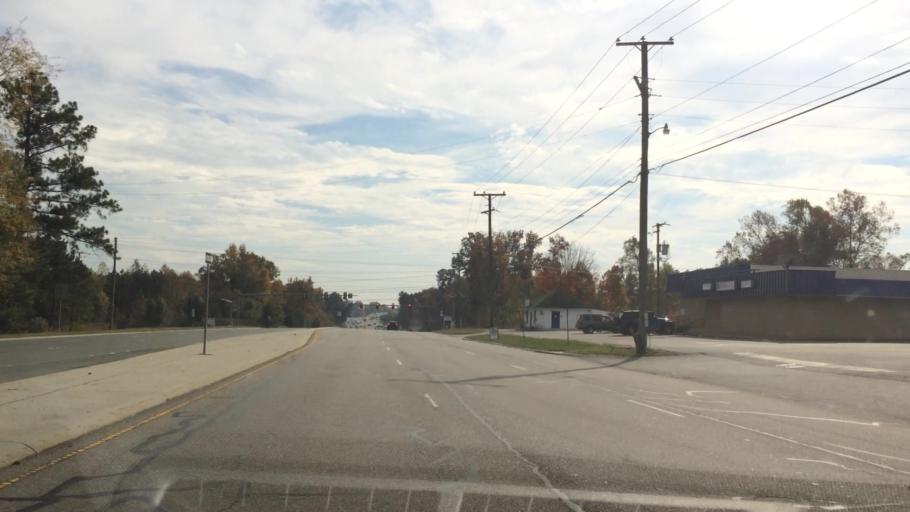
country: US
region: Virginia
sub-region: Henrico County
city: Glen Allen
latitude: 37.6834
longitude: -77.4620
